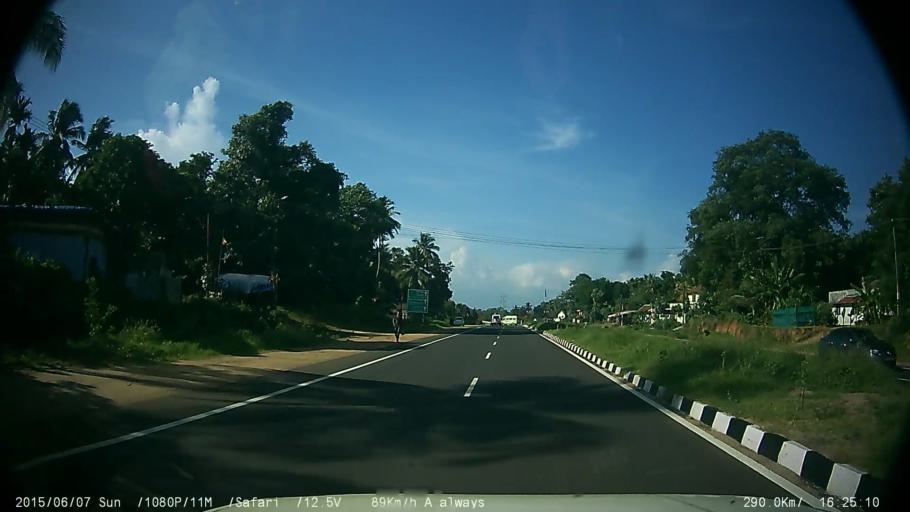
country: IN
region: Kerala
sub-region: Palakkad district
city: Palakkad
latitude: 10.7000
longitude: 76.5910
